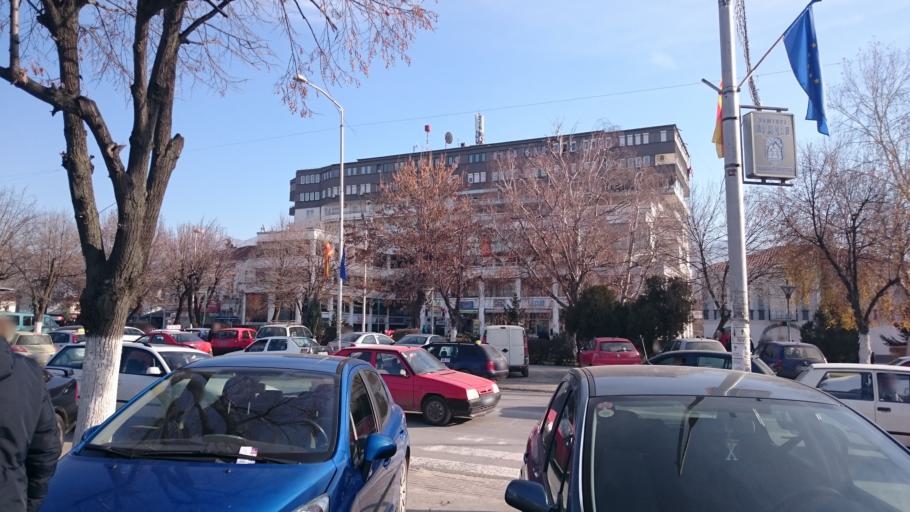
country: MK
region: Prilep
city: Prilep
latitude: 41.3455
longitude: 21.5520
